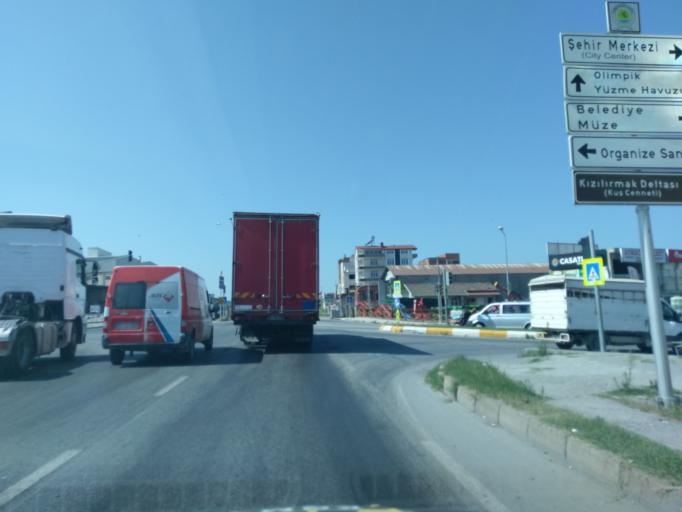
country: TR
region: Samsun
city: Bafra
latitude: 41.5647
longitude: 35.8868
